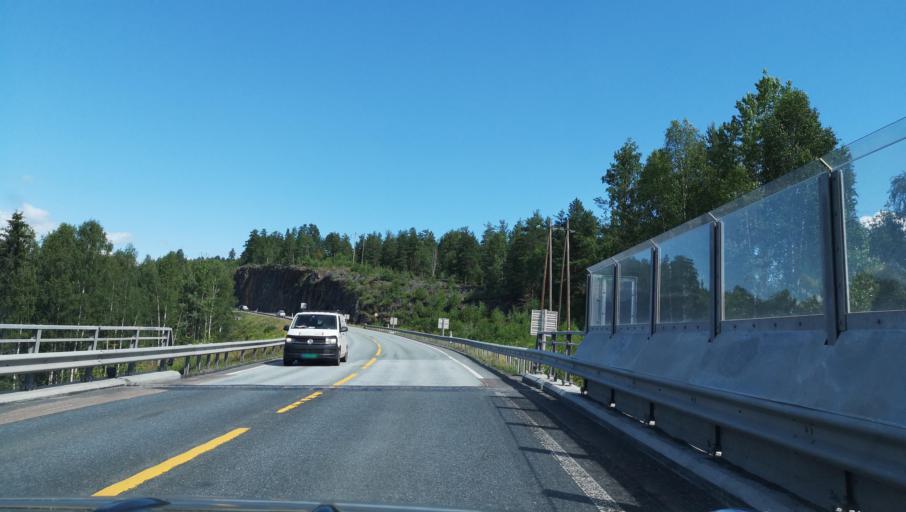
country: NO
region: Buskerud
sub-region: Modum
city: Vikersund
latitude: 59.9311
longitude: 9.9627
